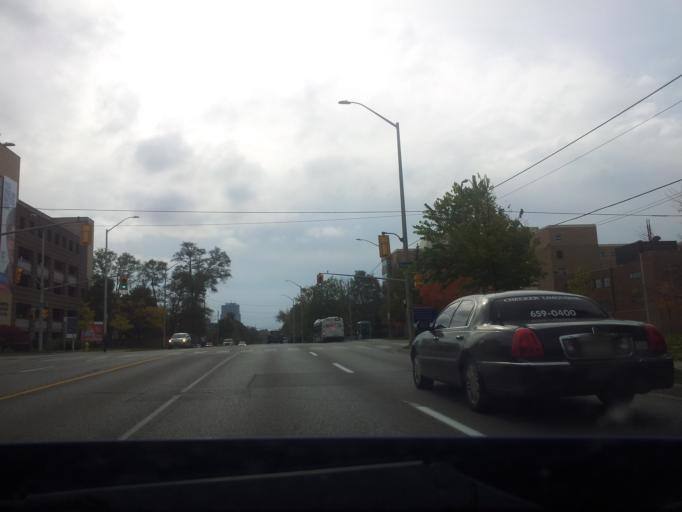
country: CA
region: Ontario
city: London
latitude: 43.0000
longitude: -81.2556
